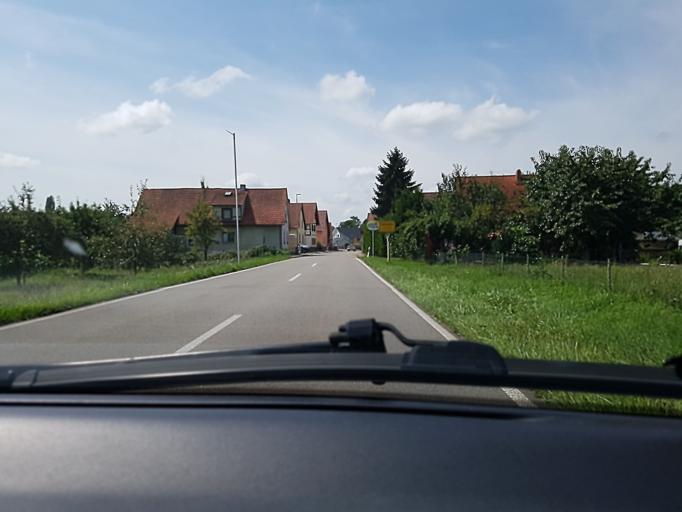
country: DE
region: Baden-Wuerttemberg
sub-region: Freiburg Region
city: Willstatt
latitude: 48.5602
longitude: 7.8826
